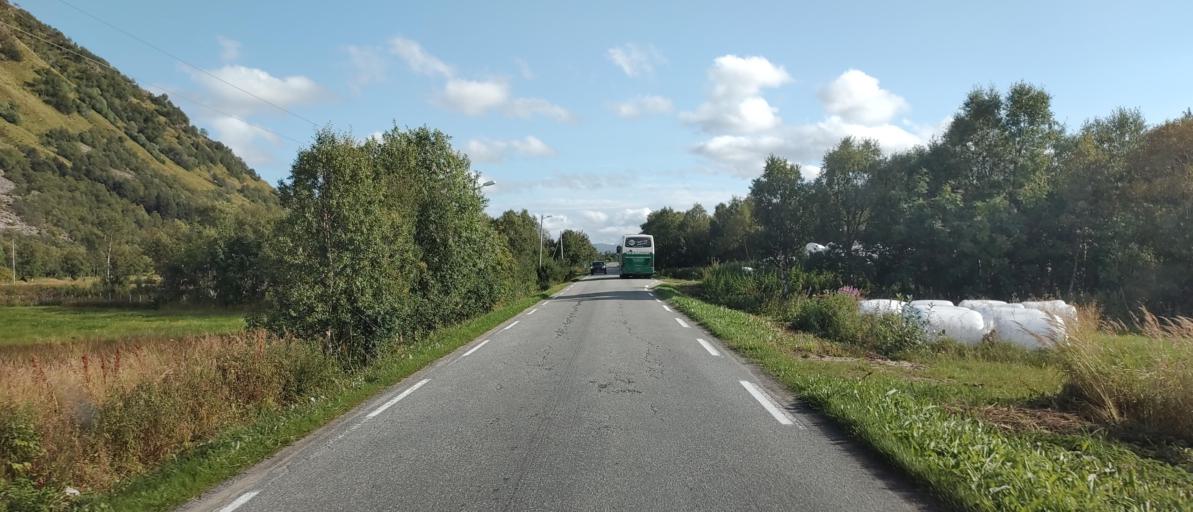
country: NO
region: Nordland
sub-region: Sortland
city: Sortland
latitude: 69.0362
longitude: 15.5224
